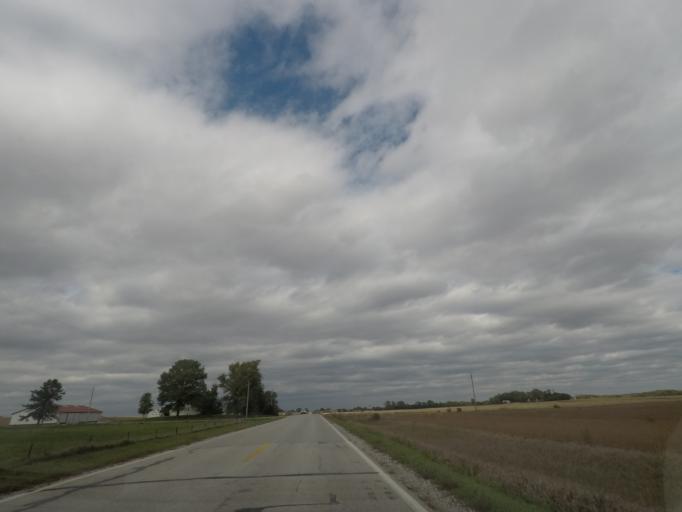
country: US
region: Iowa
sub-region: Story County
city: Huxley
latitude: 41.8484
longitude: -93.5315
